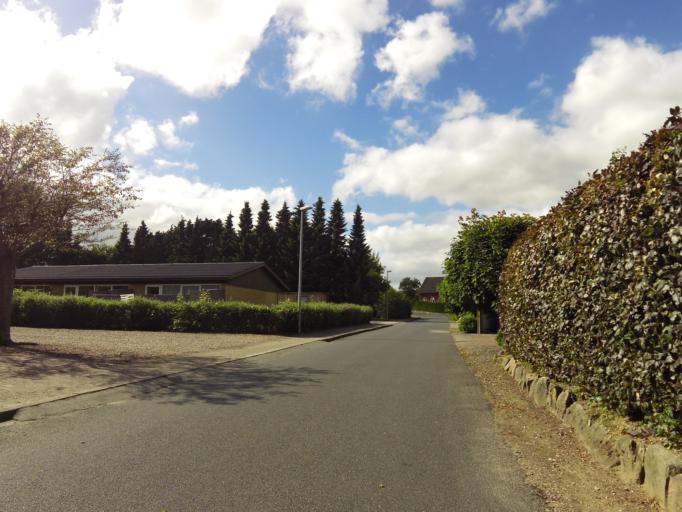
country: DK
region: South Denmark
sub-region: Kolding Kommune
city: Vamdrup
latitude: 55.3590
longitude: 9.2025
